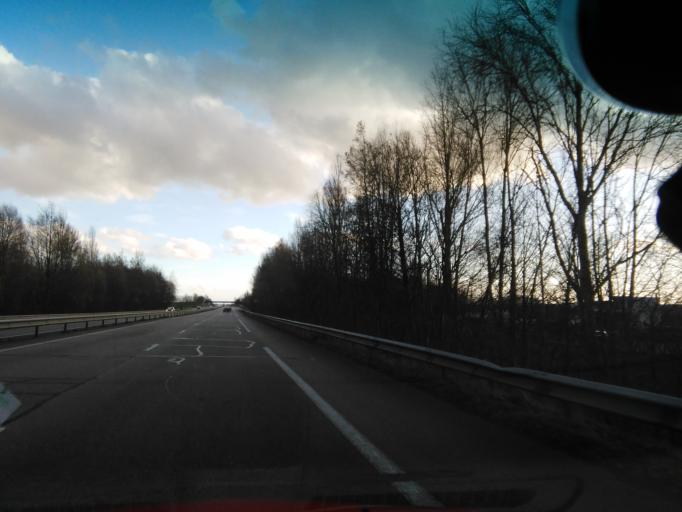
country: FR
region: Lower Normandy
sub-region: Departement du Calvados
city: Potigny
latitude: 48.9371
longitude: -0.2091
